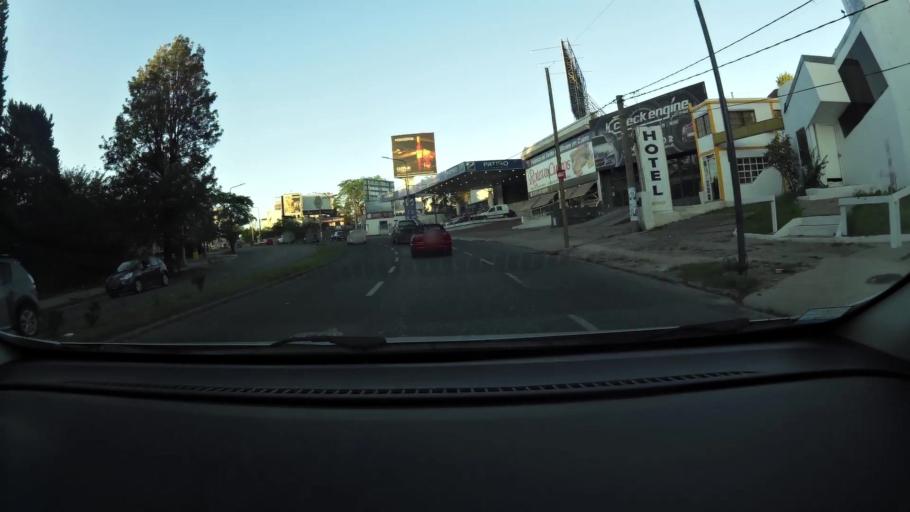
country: AR
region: Cordoba
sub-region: Departamento de Capital
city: Cordoba
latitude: -31.3811
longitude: -64.2233
